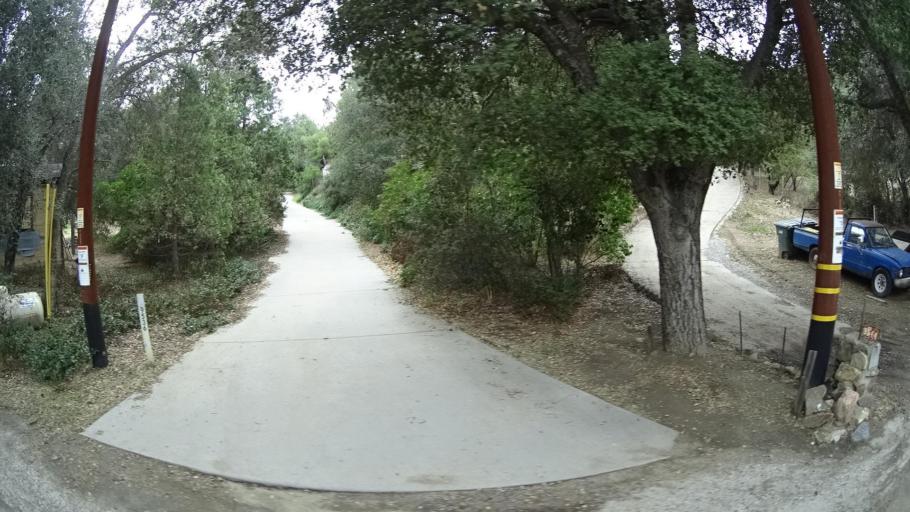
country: US
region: California
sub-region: San Diego County
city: Descanso
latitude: 32.8571
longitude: -116.6177
